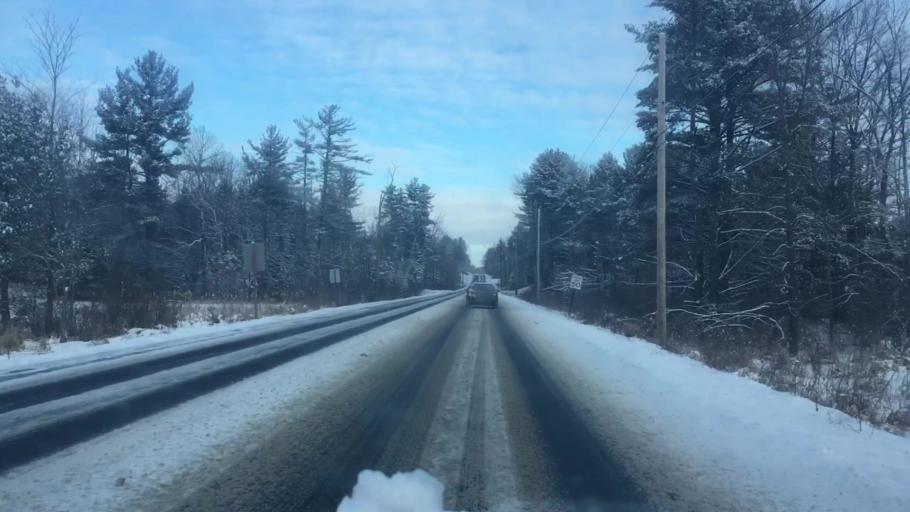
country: US
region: Maine
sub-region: Cumberland County
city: North Windham
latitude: 43.8013
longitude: -70.4403
